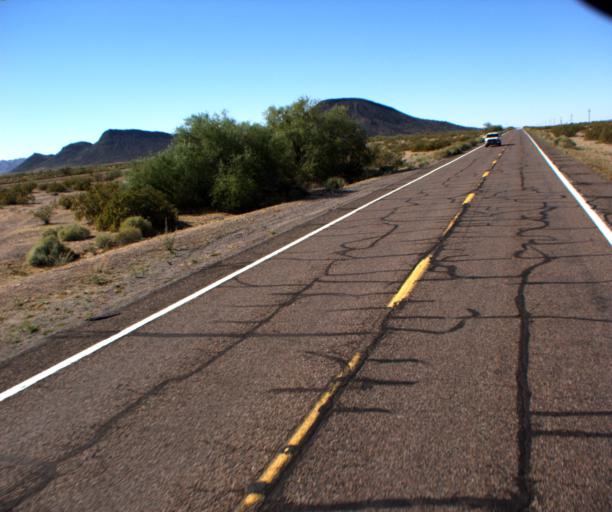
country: US
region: Arizona
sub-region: Maricopa County
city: Gila Bend
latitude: 32.7771
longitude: -112.8124
